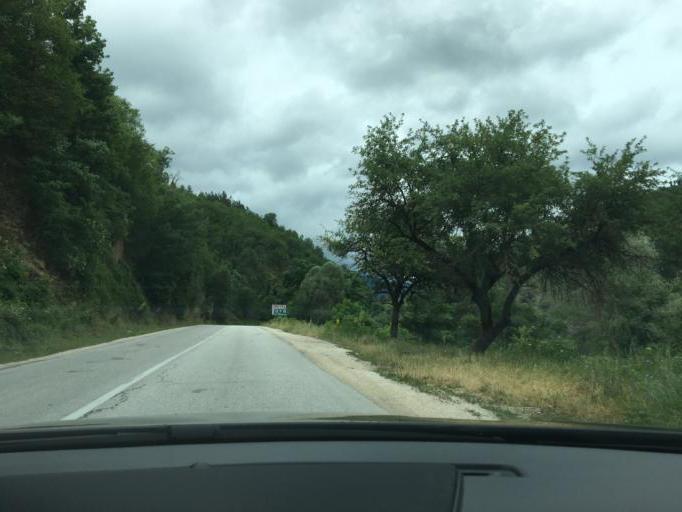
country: MK
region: Kriva Palanka
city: Kriva Palanka
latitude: 42.2294
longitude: 22.3613
